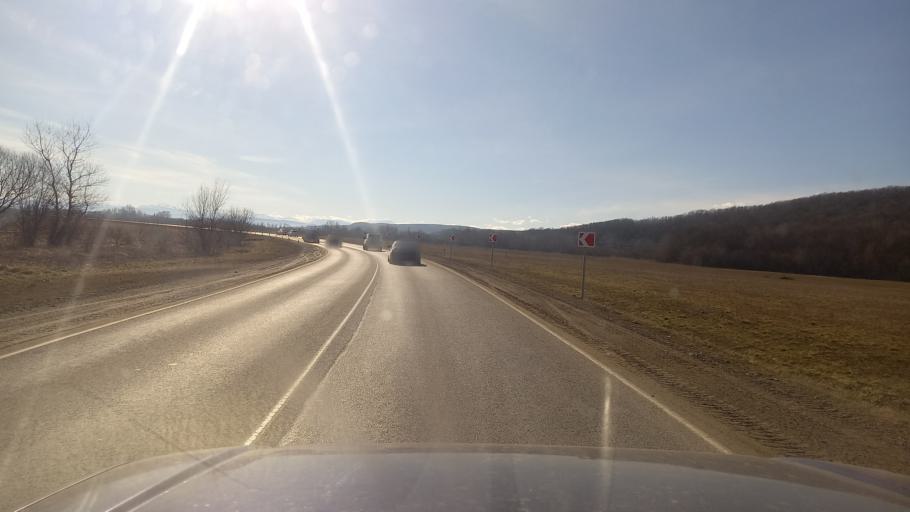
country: RU
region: Adygeya
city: Tul'skiy
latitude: 44.5232
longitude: 40.1352
